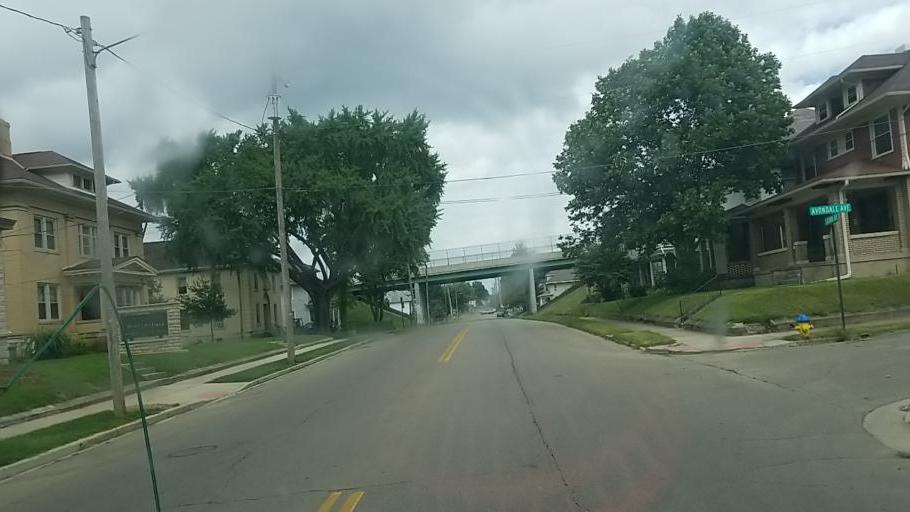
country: US
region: Ohio
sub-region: Clark County
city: Springfield
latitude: 39.9255
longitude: -83.7952
